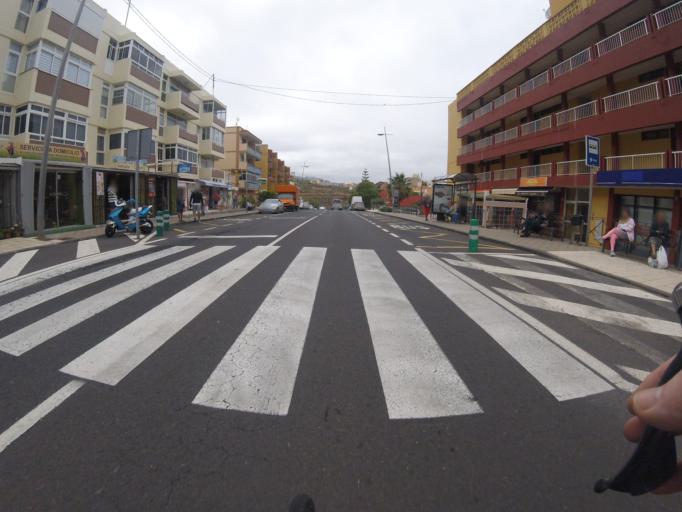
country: ES
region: Canary Islands
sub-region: Provincia de Santa Cruz de Tenerife
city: Tegueste
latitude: 28.5539
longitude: -16.3447
